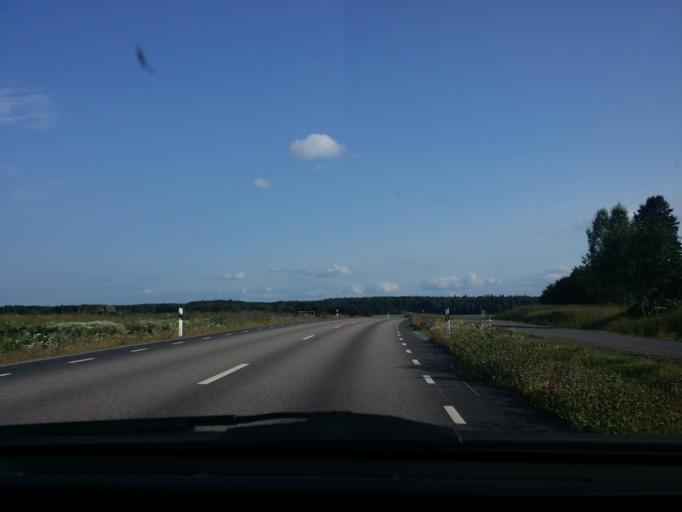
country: SE
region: Vaestmanland
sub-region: Vasteras
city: Tillberga
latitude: 59.5916
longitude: 16.6661
